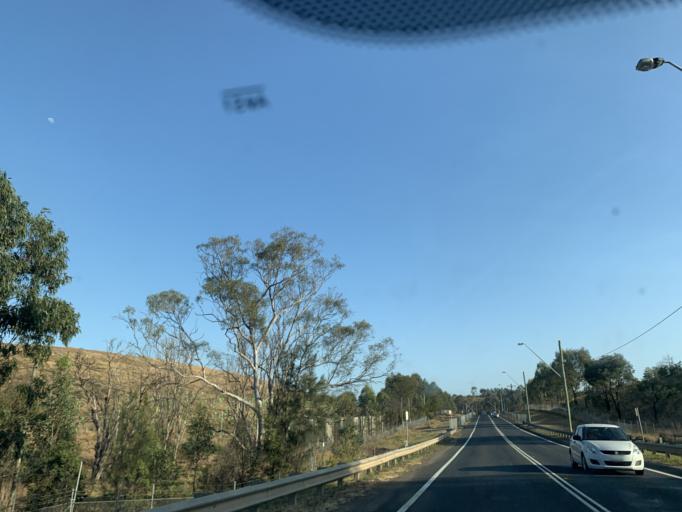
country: AU
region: New South Wales
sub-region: Fairfield
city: Horsley Park
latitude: -33.8139
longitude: 150.8657
